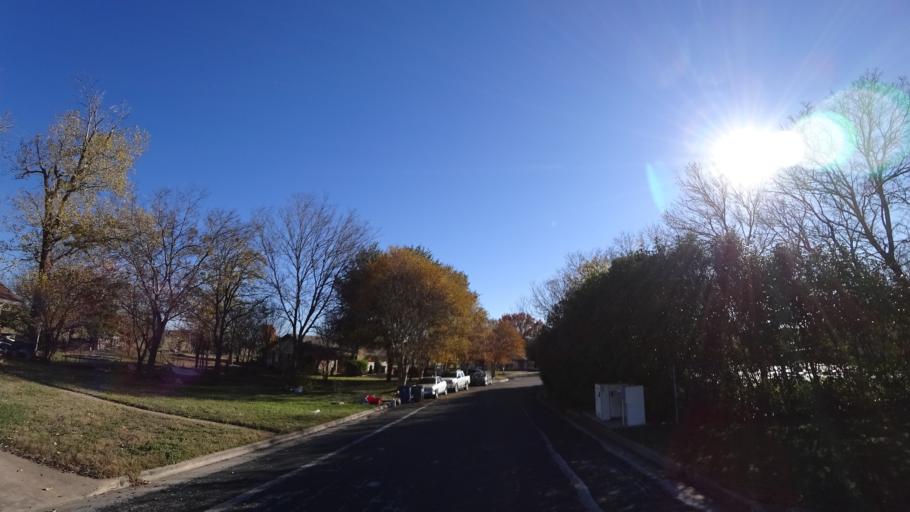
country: US
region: Texas
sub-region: Travis County
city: Wells Branch
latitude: 30.4097
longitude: -97.6893
